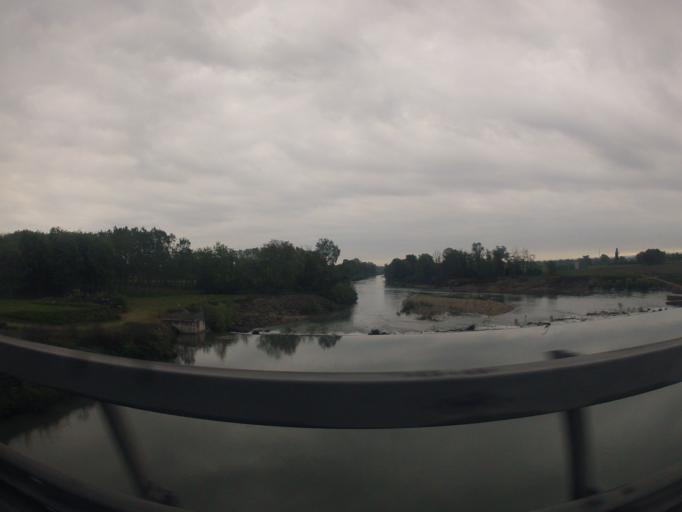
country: IT
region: Piedmont
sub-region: Provincia di Cuneo
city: Casalgrasso
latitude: 44.8270
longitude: 7.6236
